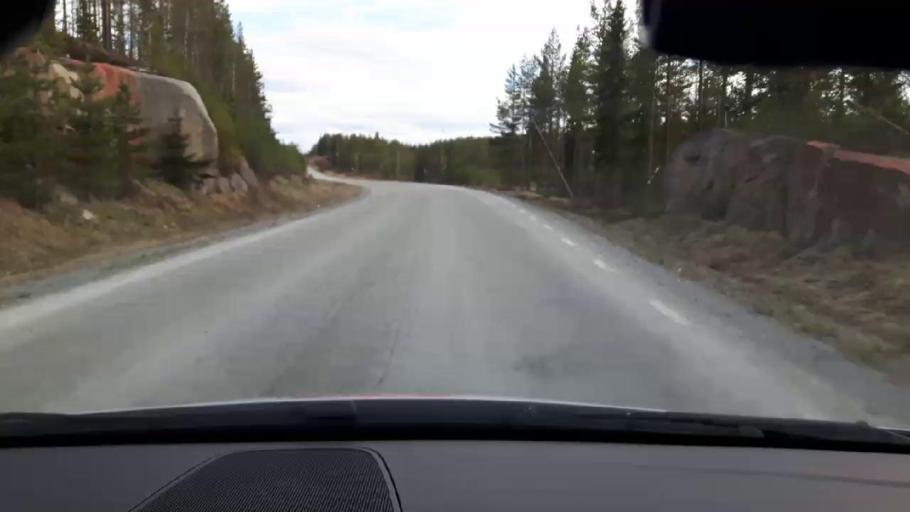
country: SE
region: Jaemtland
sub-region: Bergs Kommun
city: Hoverberg
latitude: 62.7026
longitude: 14.6205
